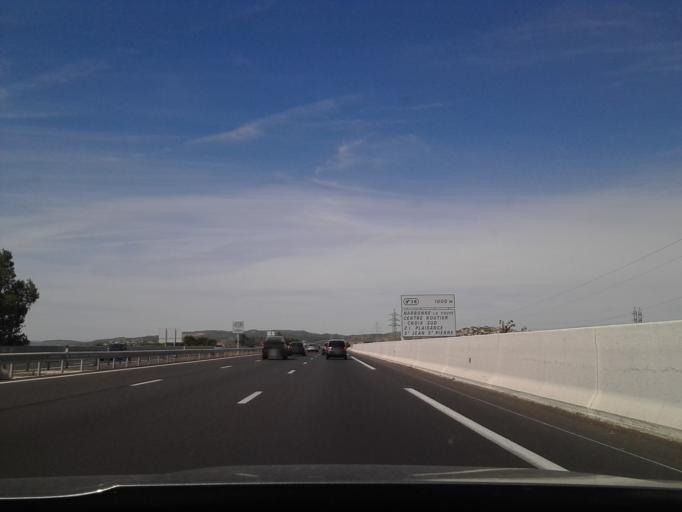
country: FR
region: Languedoc-Roussillon
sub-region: Departement de l'Aude
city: Narbonne
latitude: 43.1688
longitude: 3.0089
